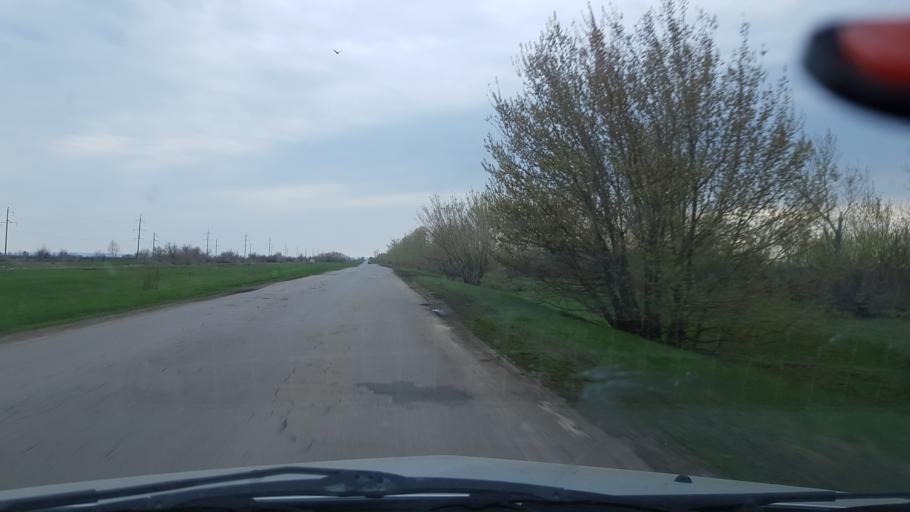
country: RU
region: Samara
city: Podstepki
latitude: 53.6677
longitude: 49.1466
